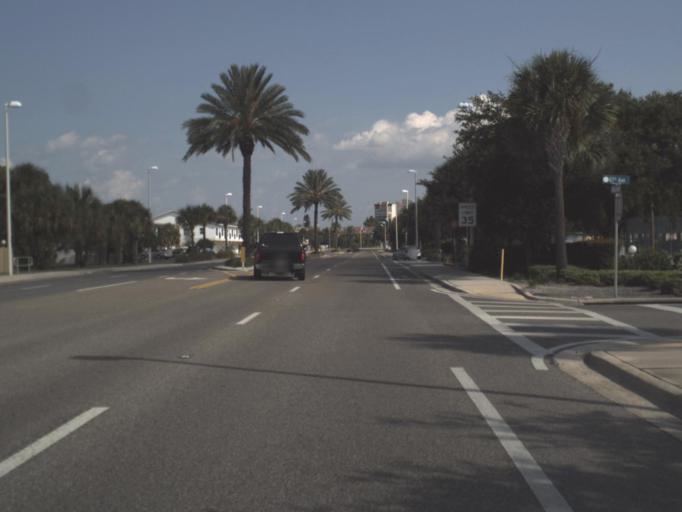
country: US
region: Florida
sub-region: Pinellas County
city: South Pasadena
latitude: 27.7508
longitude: -82.7557
